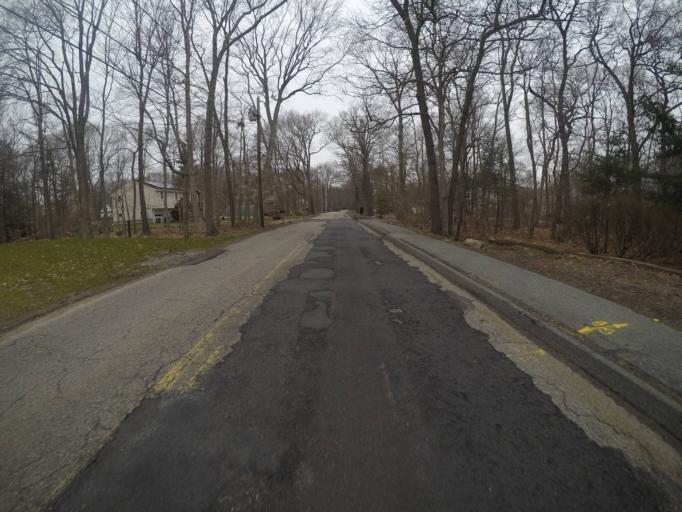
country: US
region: Massachusetts
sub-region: Bristol County
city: Easton
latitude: 42.0562
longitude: -71.1425
